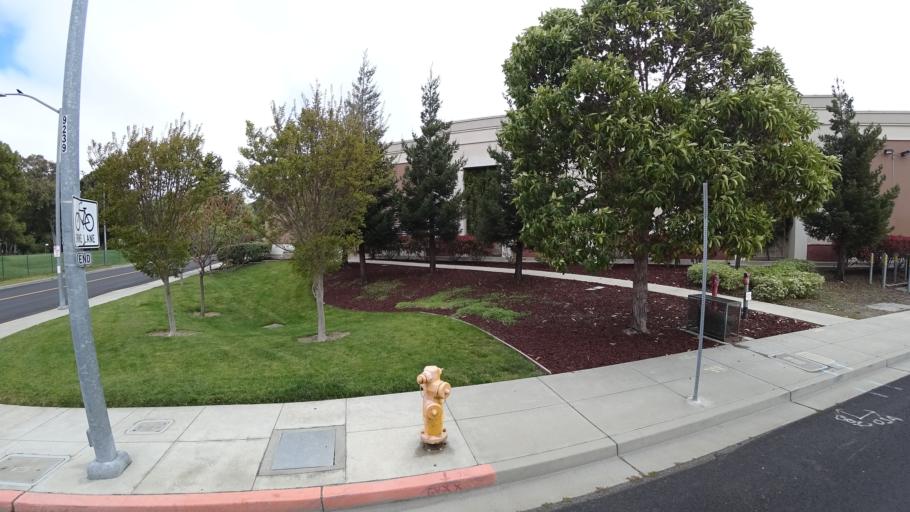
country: US
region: California
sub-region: Alameda County
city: San Lorenzo
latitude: 37.6660
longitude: -122.1220
